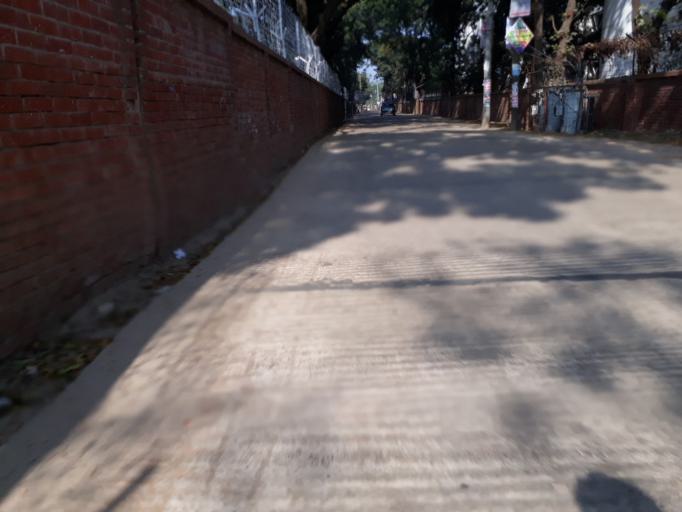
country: BD
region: Dhaka
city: Tungi
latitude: 23.8668
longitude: 90.3104
